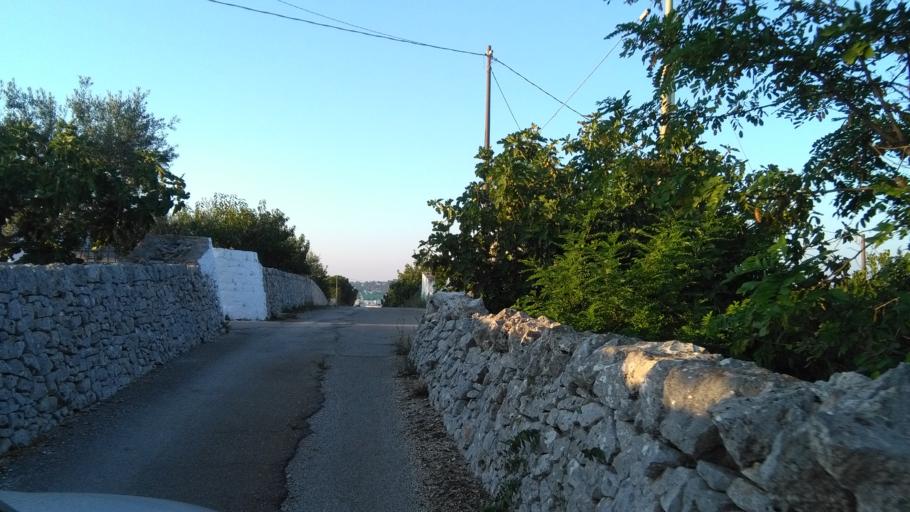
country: IT
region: Apulia
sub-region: Provincia di Bari
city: Putignano
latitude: 40.8245
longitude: 17.1031
